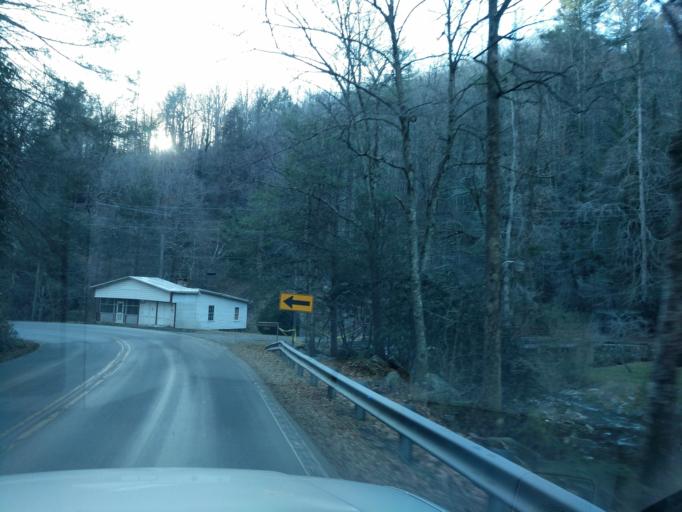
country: US
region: North Carolina
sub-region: Henderson County
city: Edneyville
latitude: 35.4548
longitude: -82.2976
